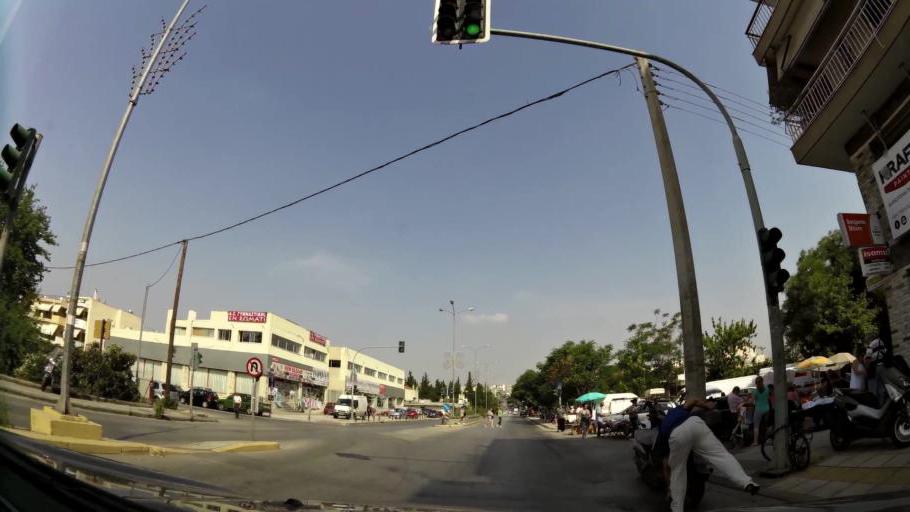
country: GR
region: Central Macedonia
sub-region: Nomos Thessalonikis
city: Stavroupoli
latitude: 40.6639
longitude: 22.9325
